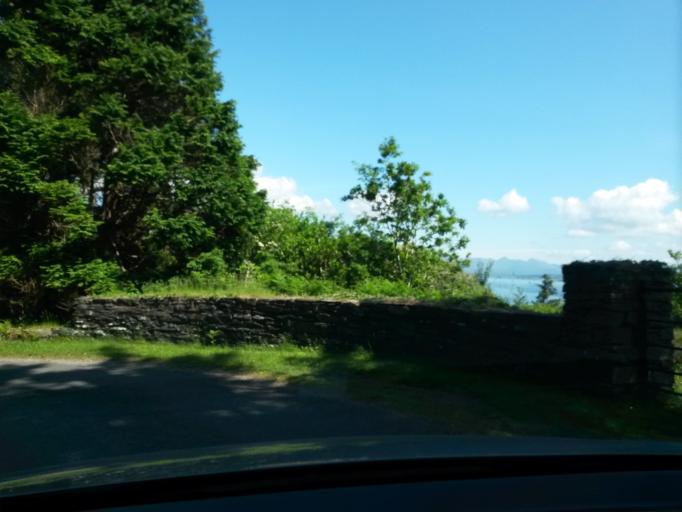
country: IE
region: Munster
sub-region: Ciarrai
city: Cahersiveen
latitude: 51.7375
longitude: -9.9399
